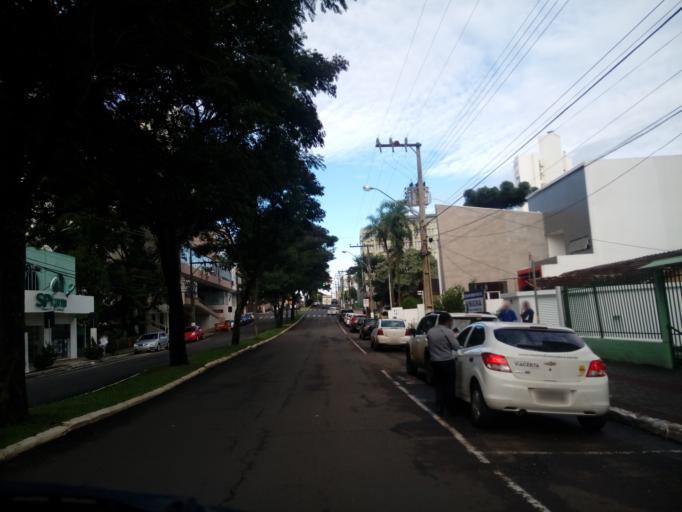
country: BR
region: Santa Catarina
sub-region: Chapeco
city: Chapeco
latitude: -27.1040
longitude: -52.6112
